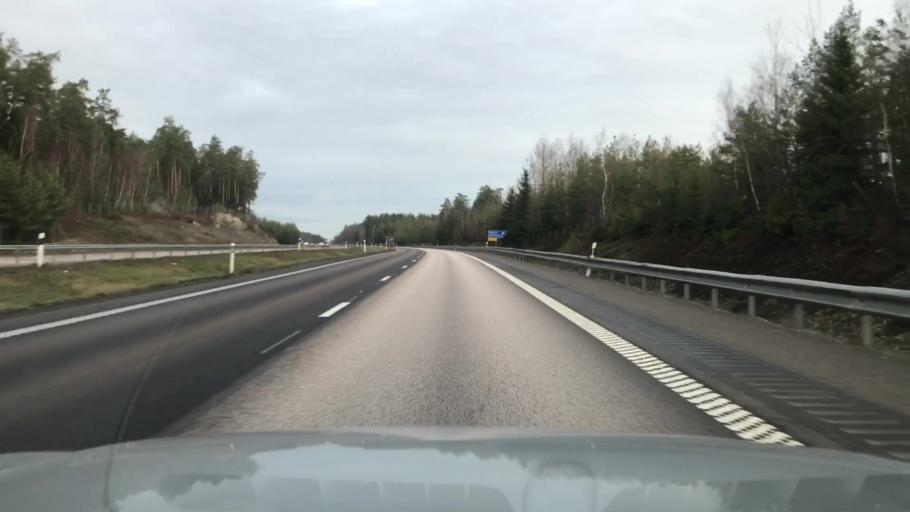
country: SE
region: Soedermanland
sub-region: Trosa Kommun
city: Vagnharad
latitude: 59.0202
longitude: 17.5529
